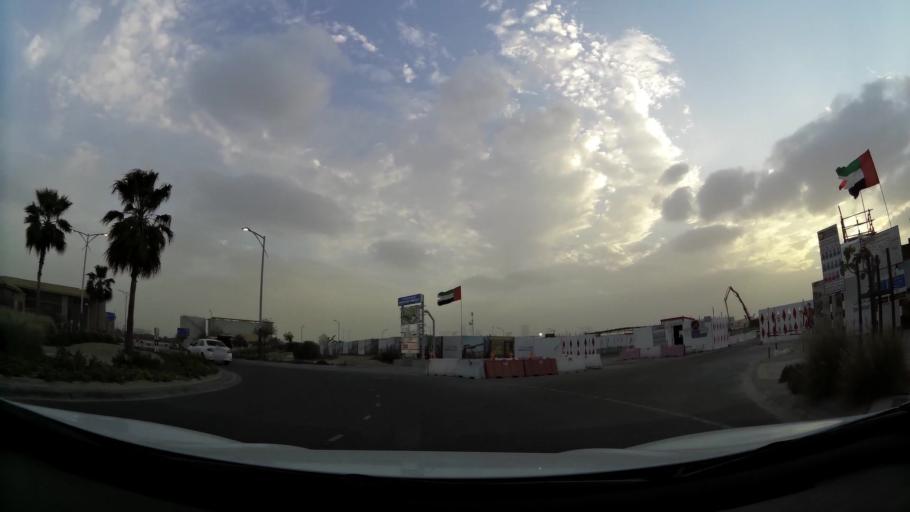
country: AE
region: Abu Dhabi
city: Abu Dhabi
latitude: 24.5348
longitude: 54.4277
